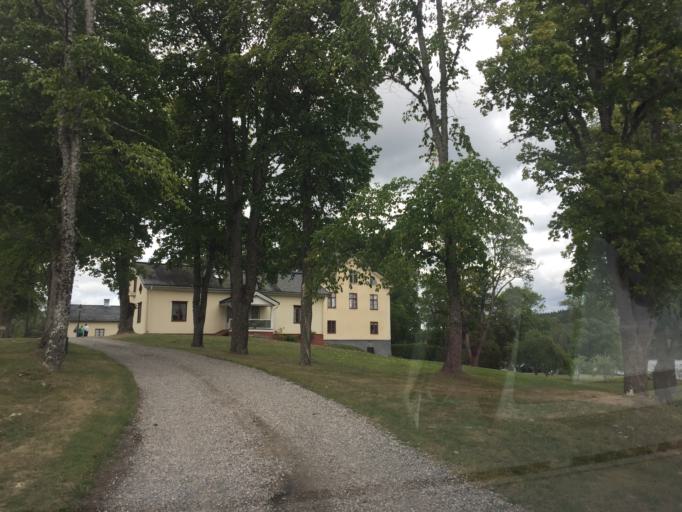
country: SE
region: OErebro
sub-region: Hallefors Kommun
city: Haellefors
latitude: 59.7904
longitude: 14.3624
